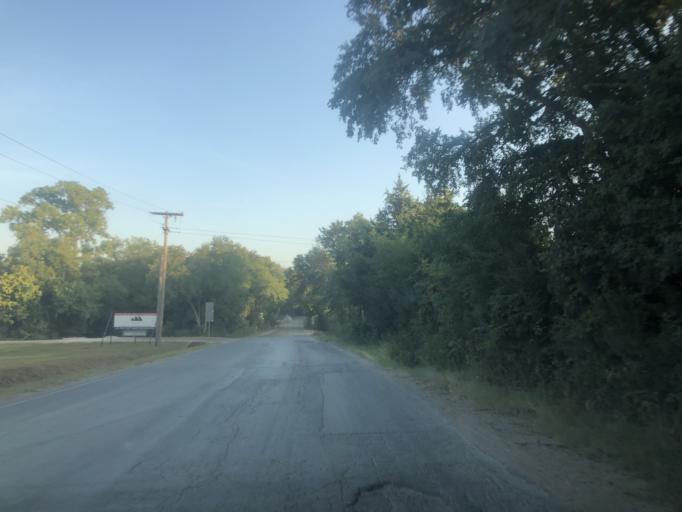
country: US
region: Texas
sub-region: Tarrant County
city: Lakeside
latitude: 32.7916
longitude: -97.4918
